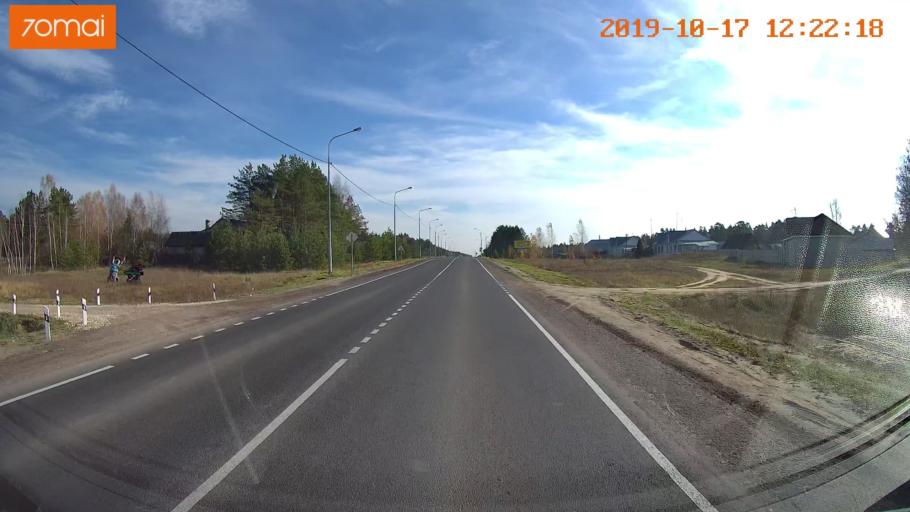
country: RU
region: Rjazan
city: Gus'-Zheleznyy
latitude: 55.0529
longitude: 41.1694
